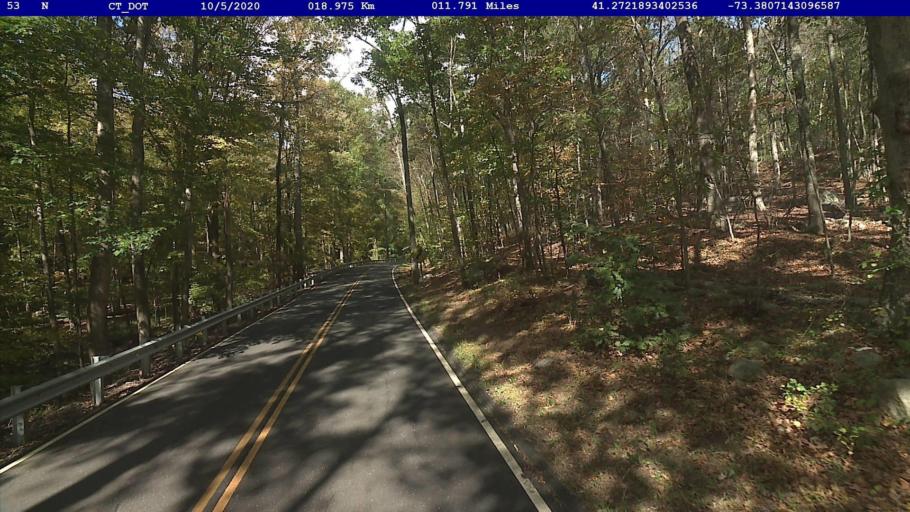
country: US
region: Connecticut
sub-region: Fairfield County
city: Georgetown
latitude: 41.2722
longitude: -73.3807
